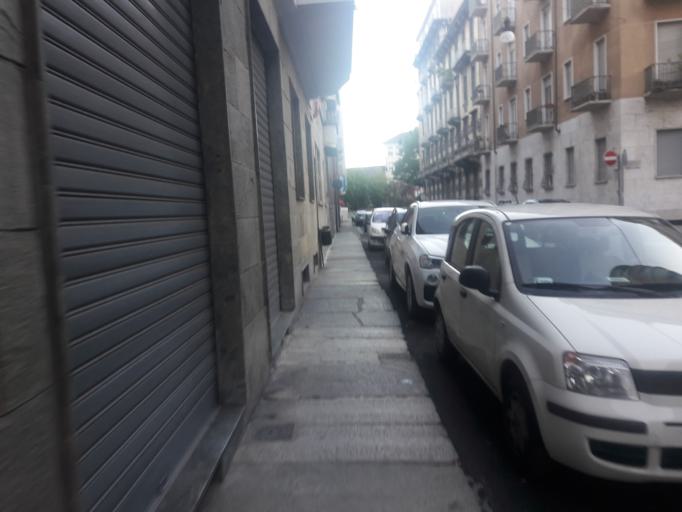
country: IT
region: Piedmont
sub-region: Provincia di Torino
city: Turin
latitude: 45.0534
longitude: 7.6674
